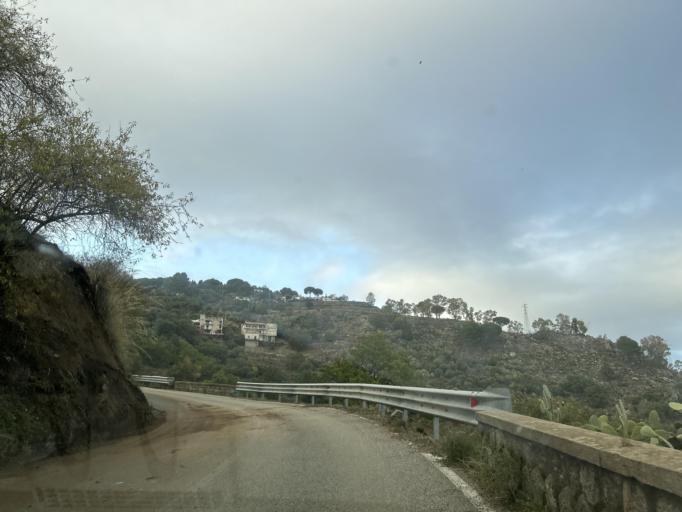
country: IT
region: Calabria
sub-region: Provincia di Catanzaro
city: Squillace Lido
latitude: 38.7592
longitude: 16.5644
